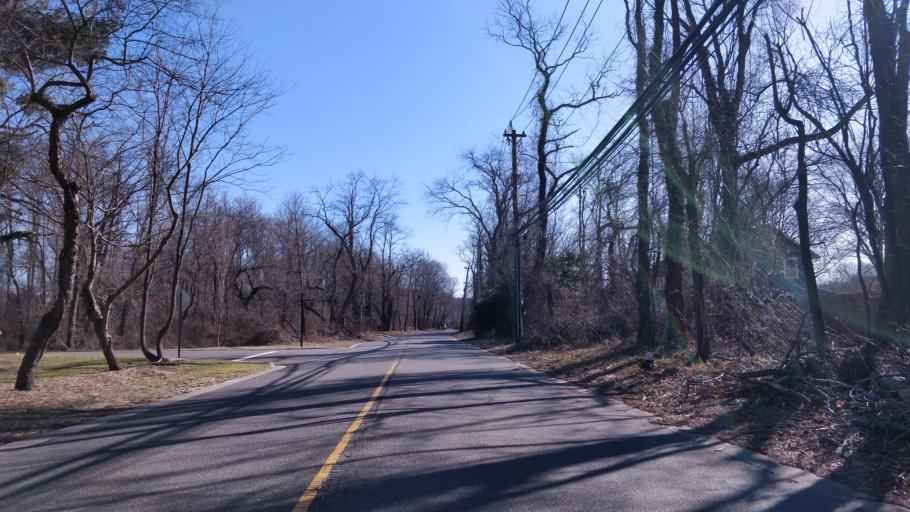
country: US
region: New York
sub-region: Nassau County
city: Old Brookville
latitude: 40.8121
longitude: -73.6009
